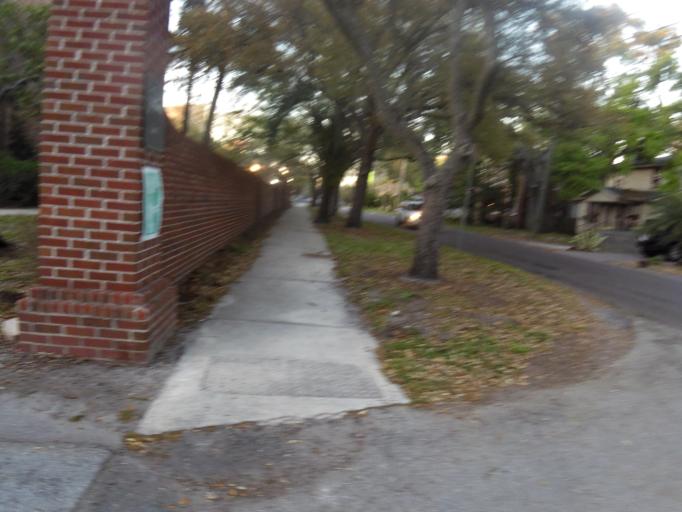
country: US
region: Florida
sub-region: Duval County
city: Jacksonville
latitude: 30.3099
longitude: -81.6623
